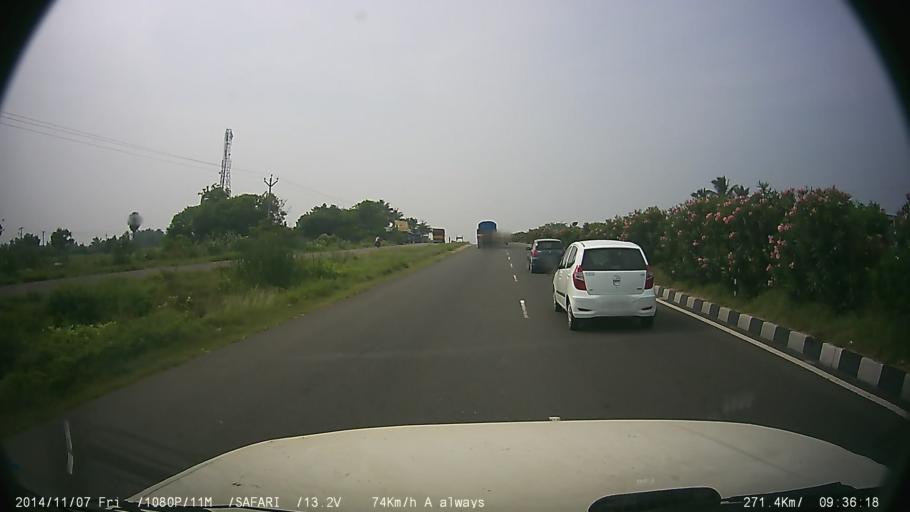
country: IN
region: Tamil Nadu
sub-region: Erode
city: Erode
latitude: 11.3678
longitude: 77.6478
